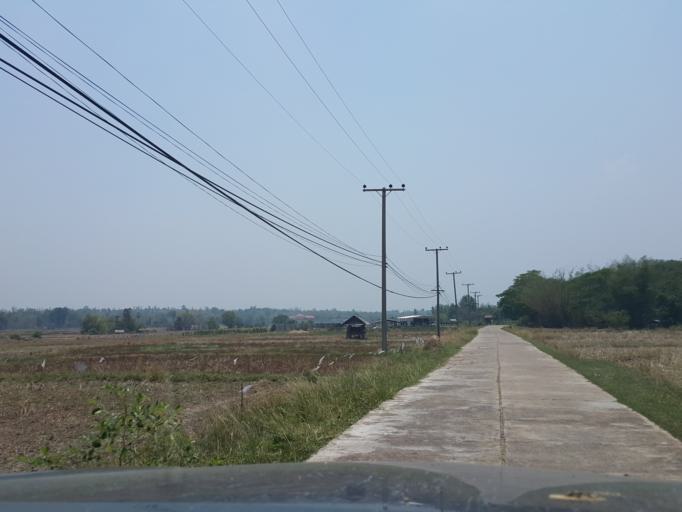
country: TH
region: Lampang
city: Thoen
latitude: 17.6377
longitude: 99.2635
